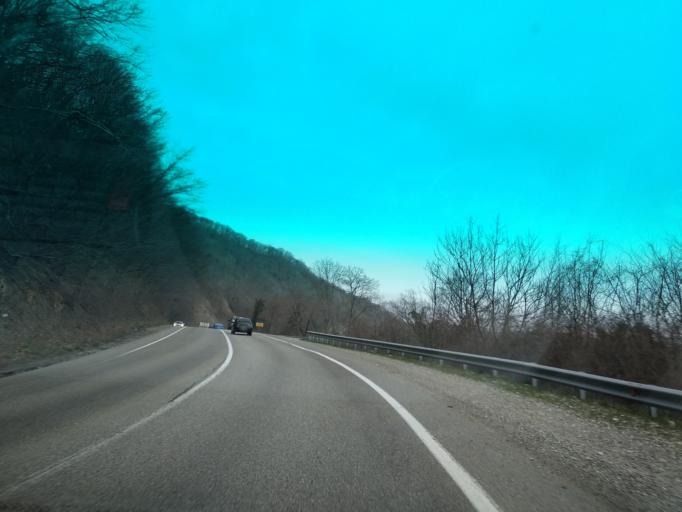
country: RU
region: Krasnodarskiy
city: Ol'ginka
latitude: 44.2220
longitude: 38.8952
